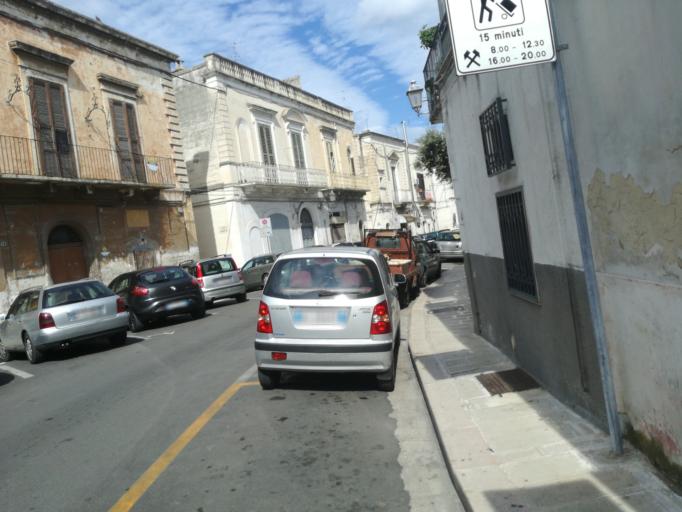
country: IT
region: Apulia
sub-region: Provincia di Bari
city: Triggiano
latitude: 41.0641
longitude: 16.9207
